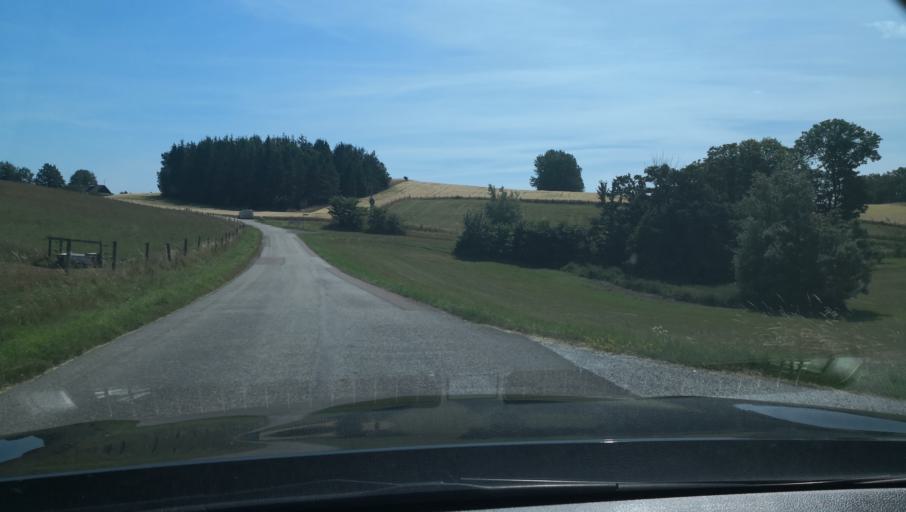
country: SE
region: Skane
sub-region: Ystads Kommun
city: Kopingebro
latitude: 55.3922
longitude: 14.1385
